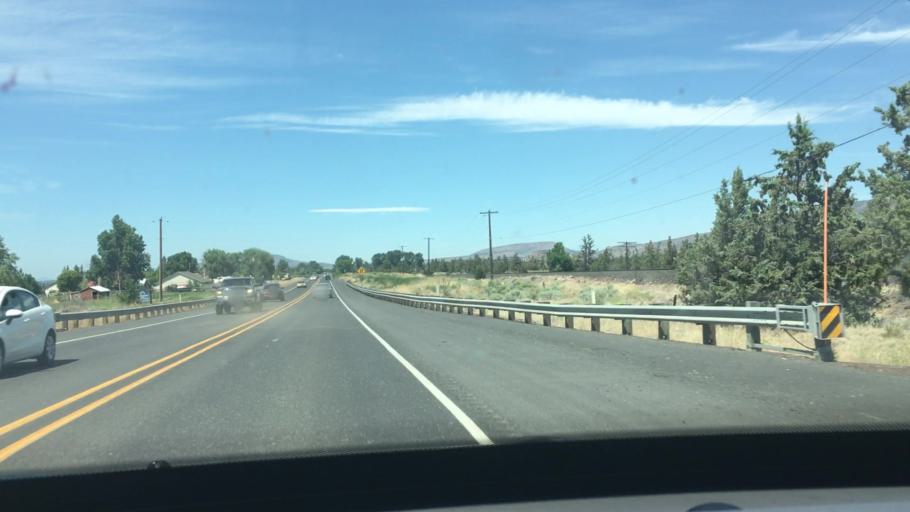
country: US
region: Oregon
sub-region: Deschutes County
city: Terrebonne
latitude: 44.3304
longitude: -121.1766
